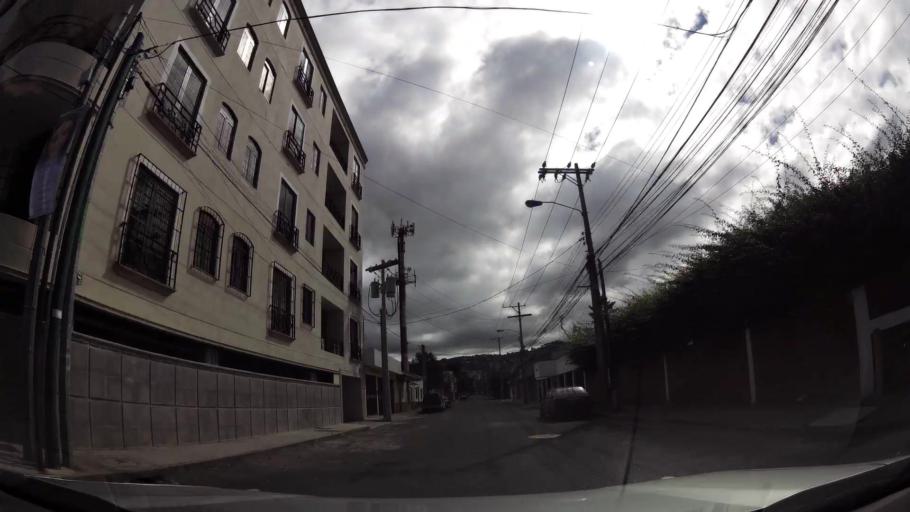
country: GT
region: Guatemala
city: Santa Catarina Pinula
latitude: 14.5914
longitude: -90.5064
